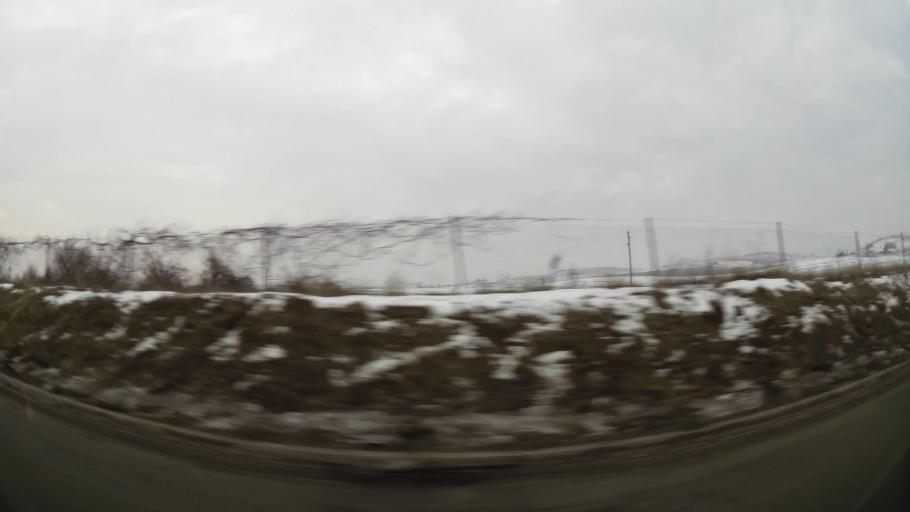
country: MK
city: Kondovo
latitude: 42.0279
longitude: 21.3300
